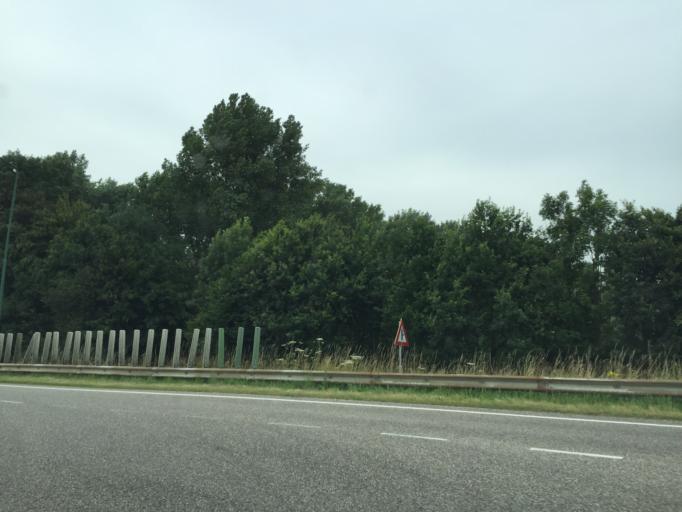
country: NL
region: North Brabant
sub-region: Gemeente Landerd
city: Reek
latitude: 51.7887
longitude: 5.6588
